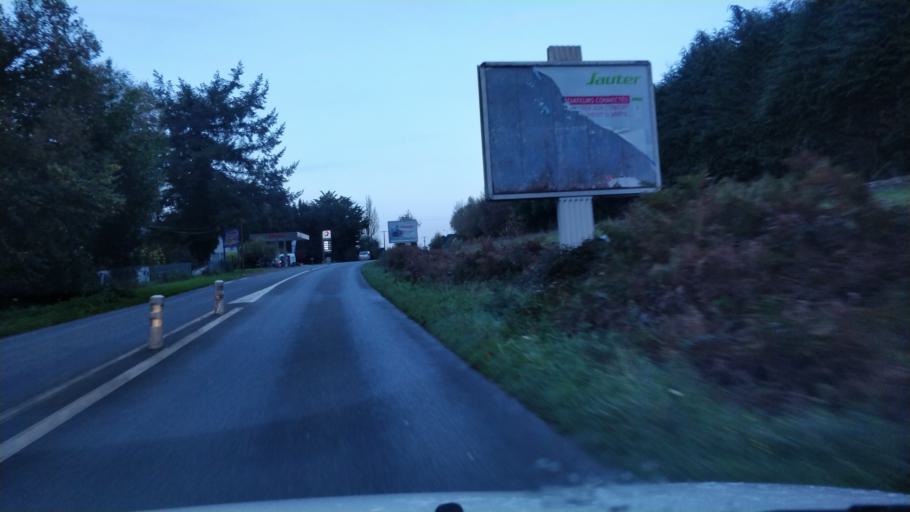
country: FR
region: Brittany
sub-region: Departement du Morbihan
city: Pontivy
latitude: 48.0801
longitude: -2.9503
